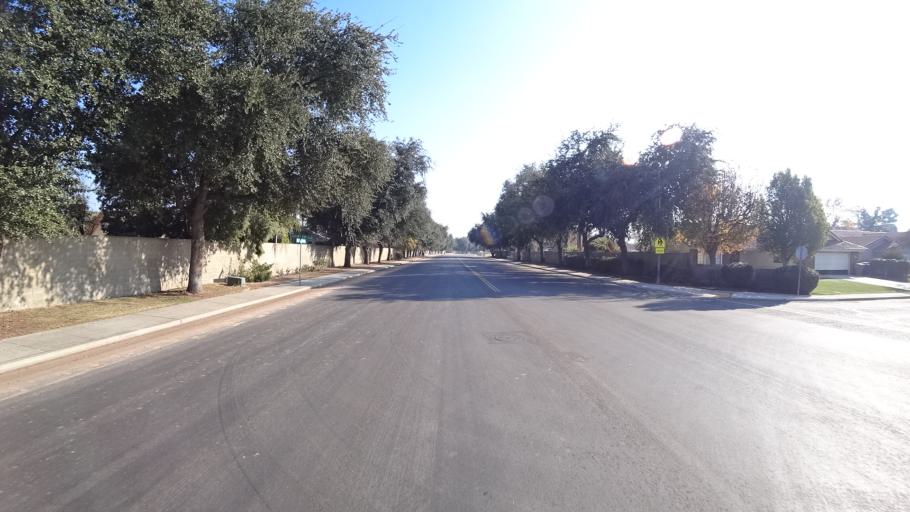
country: US
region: California
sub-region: Kern County
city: Greenacres
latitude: 35.3245
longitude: -119.1002
